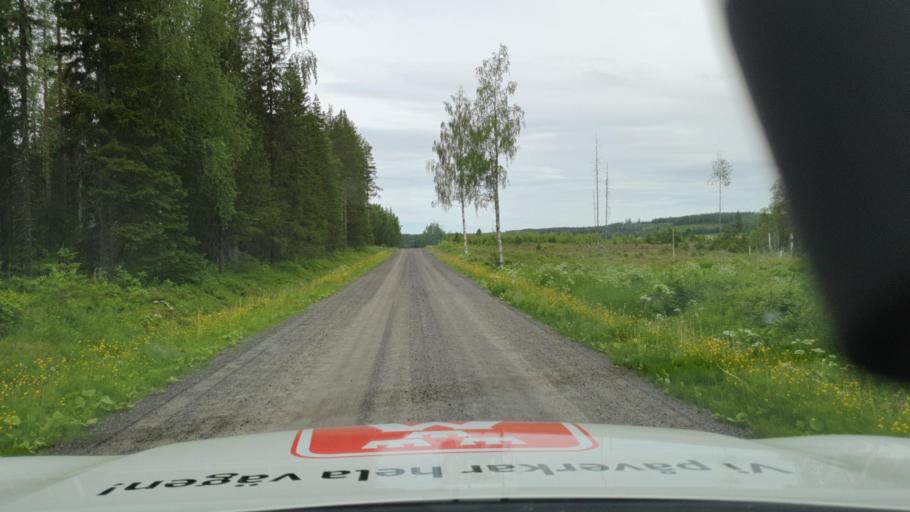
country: SE
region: Vaesterbotten
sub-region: Skelleftea Kommun
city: Burtraesk
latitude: 64.3854
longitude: 20.6137
